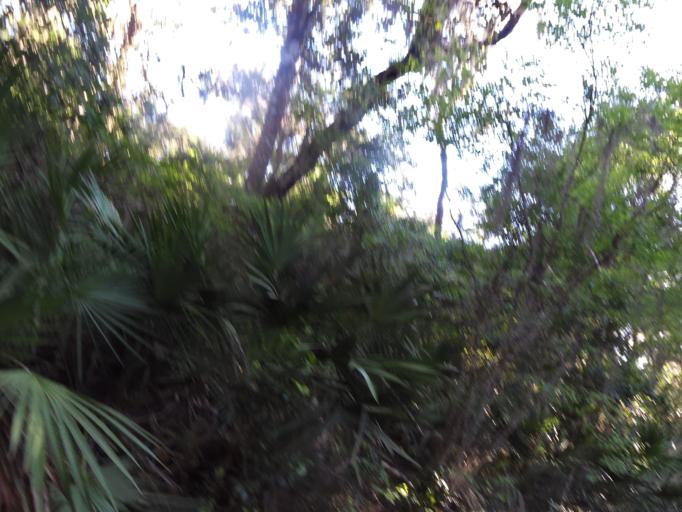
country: US
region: Florida
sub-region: Duval County
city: Atlantic Beach
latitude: 30.3797
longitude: -81.4854
